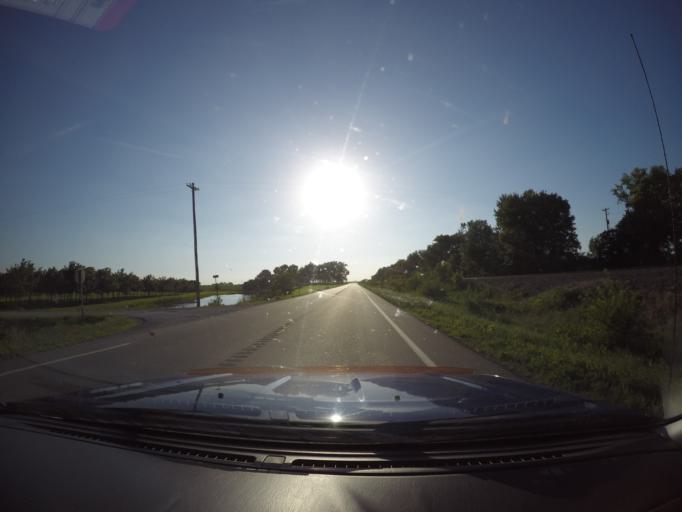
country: US
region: Kansas
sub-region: Shawnee County
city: Rossville
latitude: 39.1177
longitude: -95.9092
